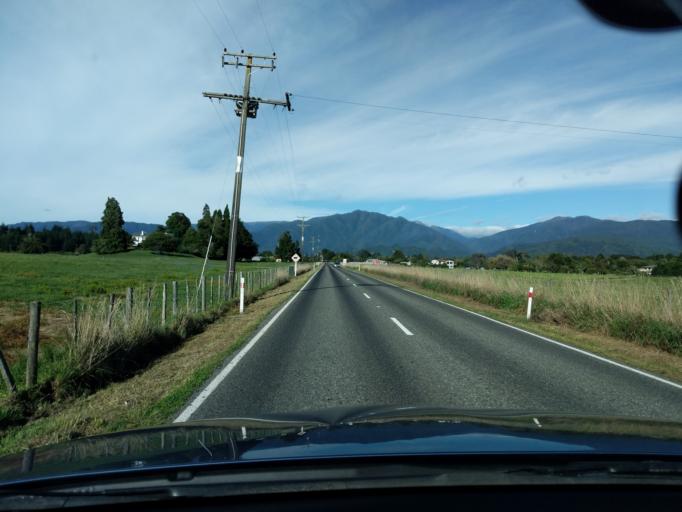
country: NZ
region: Tasman
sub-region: Tasman District
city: Takaka
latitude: -40.8524
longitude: 172.8287
